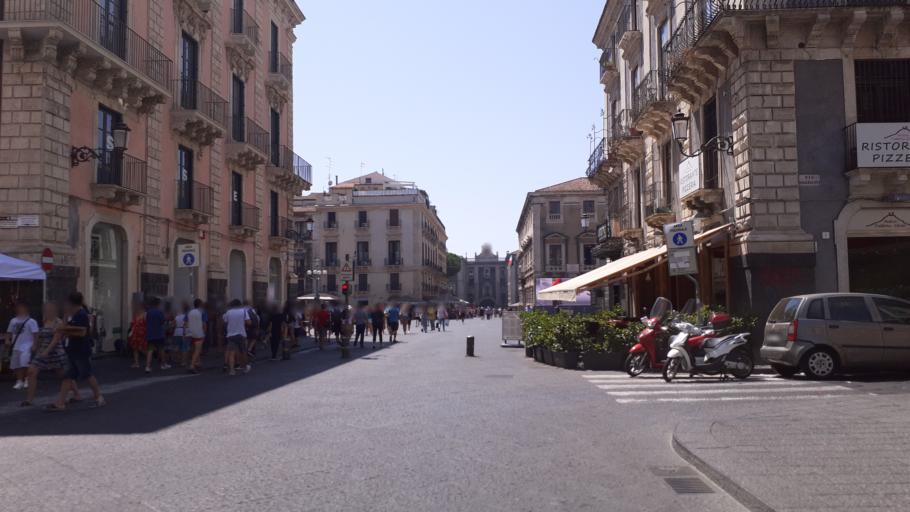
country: IT
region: Sicily
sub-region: Catania
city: Catania
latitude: 37.5043
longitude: 15.0870
